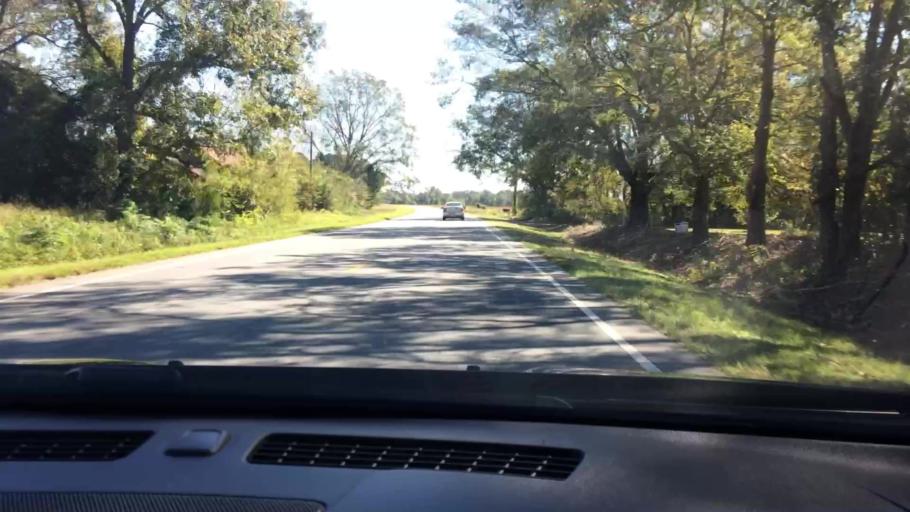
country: US
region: North Carolina
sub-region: Pitt County
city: Grifton
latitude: 35.3536
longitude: -77.3361
